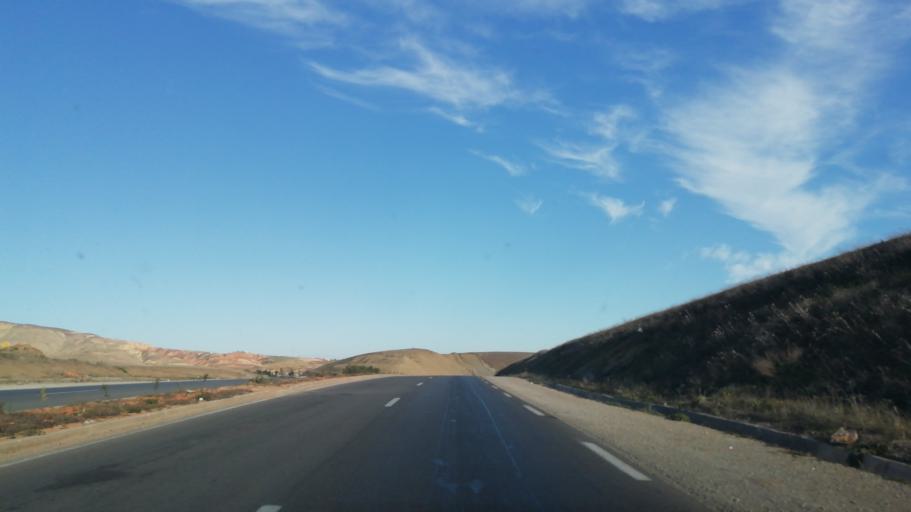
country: DZ
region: Mascara
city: Bou Hanifia el Hamamat
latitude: 35.3321
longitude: 0.0170
